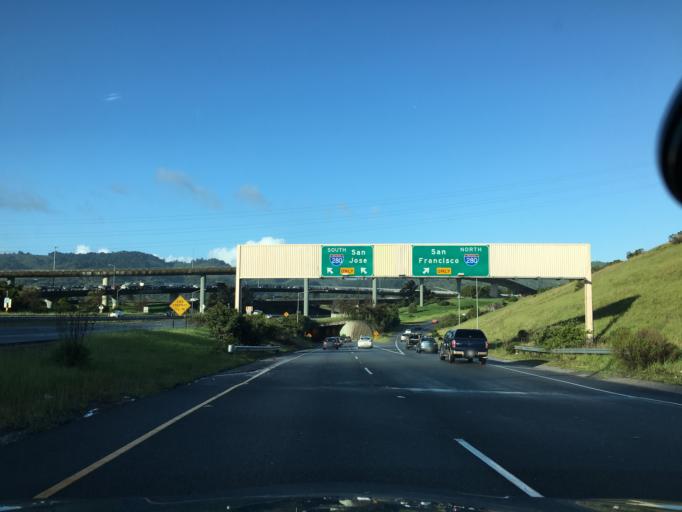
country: US
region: California
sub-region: San Mateo County
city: Highlands-Baywood Park
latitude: 37.5089
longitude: -122.3349
